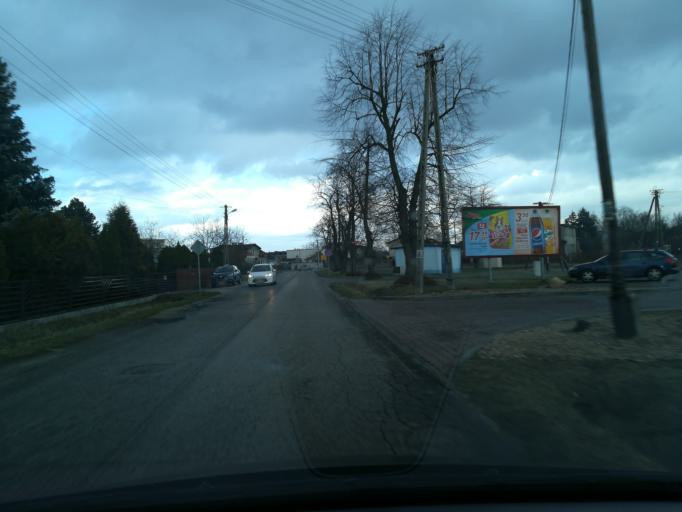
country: PL
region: Lodz Voivodeship
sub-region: Powiat radomszczanski
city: Radomsko
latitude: 51.0595
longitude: 19.4225
